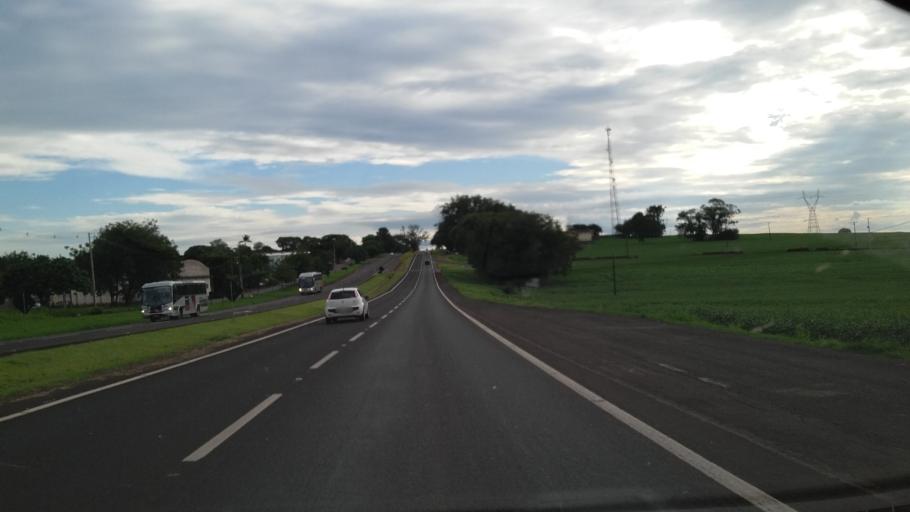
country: BR
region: Parana
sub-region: Paicandu
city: Paicandu
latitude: -23.6059
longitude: -52.0843
